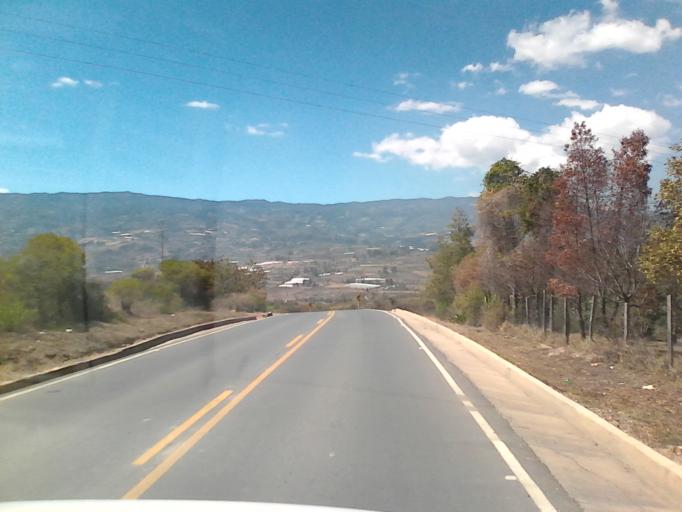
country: CO
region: Boyaca
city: Villa de Leiva
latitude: 5.6252
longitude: -73.5850
